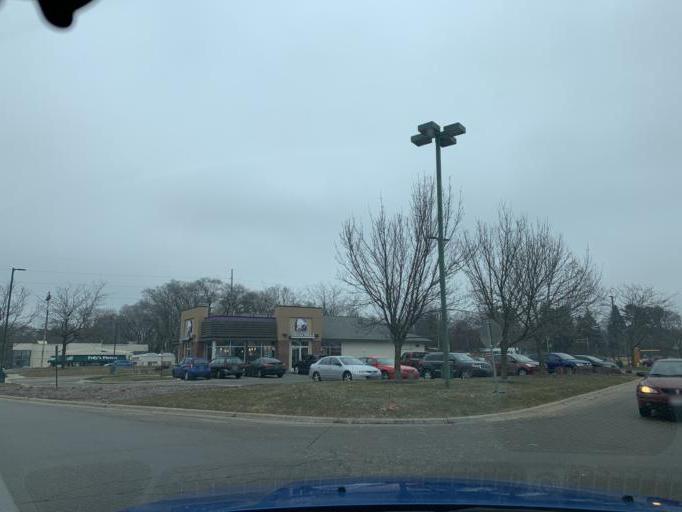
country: US
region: Wisconsin
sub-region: Dane County
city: Monona
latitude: 43.0471
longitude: -89.3230
